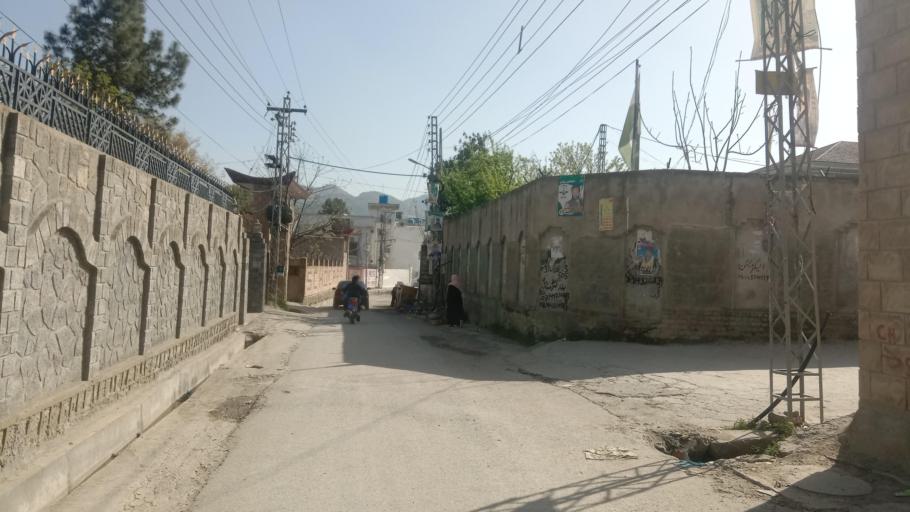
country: PK
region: Khyber Pakhtunkhwa
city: Abbottabad
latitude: 34.1731
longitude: 73.2239
